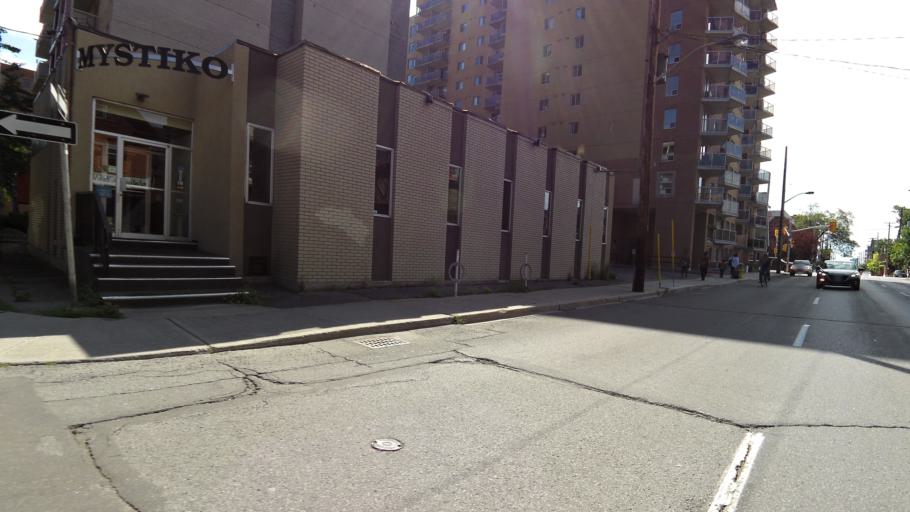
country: CA
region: Ontario
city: Ottawa
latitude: 45.4151
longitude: -75.6990
